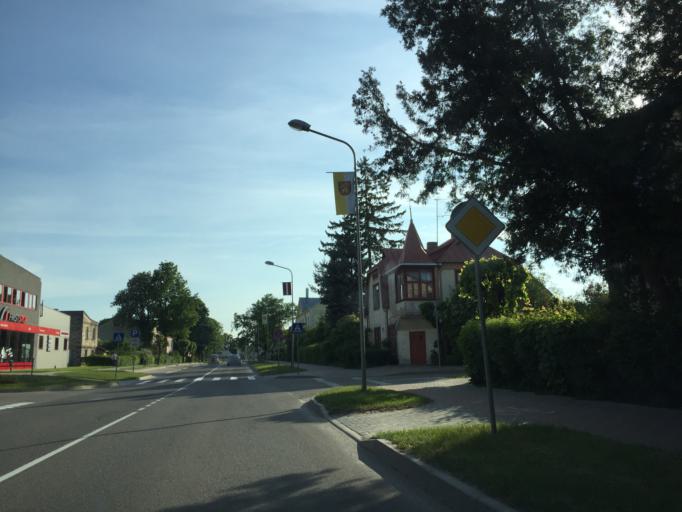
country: LV
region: Bauskas Rajons
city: Bauska
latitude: 56.4051
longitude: 24.1825
